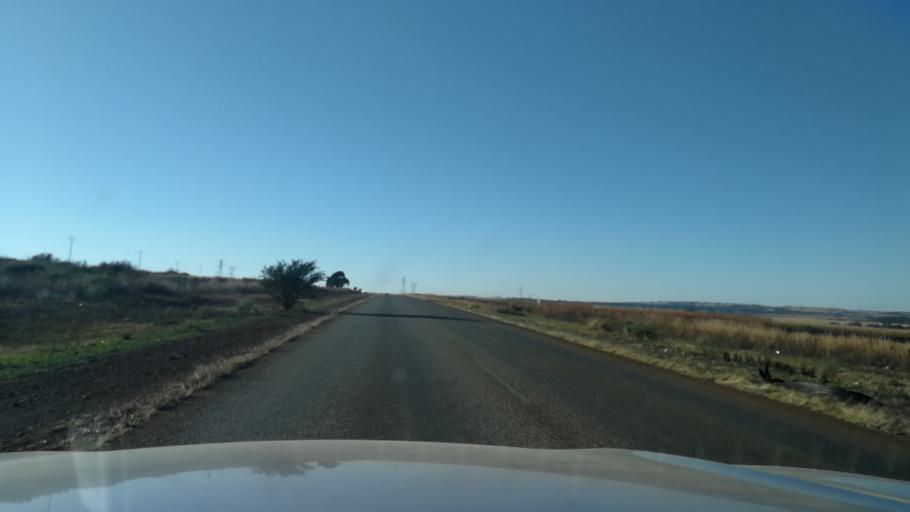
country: ZA
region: North-West
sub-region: Bojanala Platinum District Municipality
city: Rustenburg
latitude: -25.9927
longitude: 27.2901
